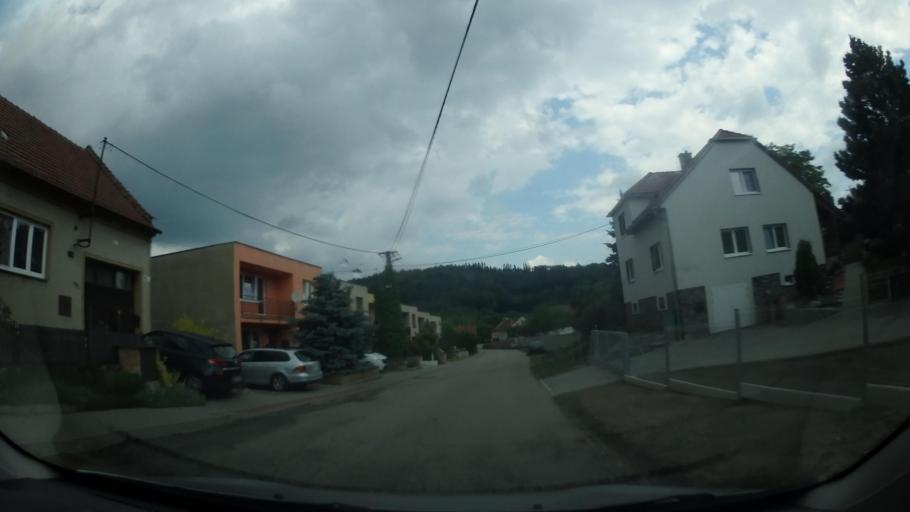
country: CZ
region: South Moravian
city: Svitavka
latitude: 49.4646
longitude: 16.6040
